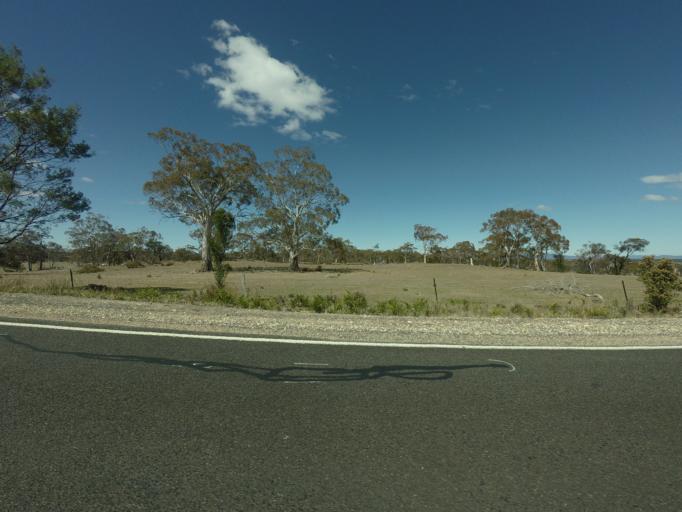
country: AU
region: Tasmania
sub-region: Break O'Day
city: St Helens
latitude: -42.0269
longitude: 148.0187
